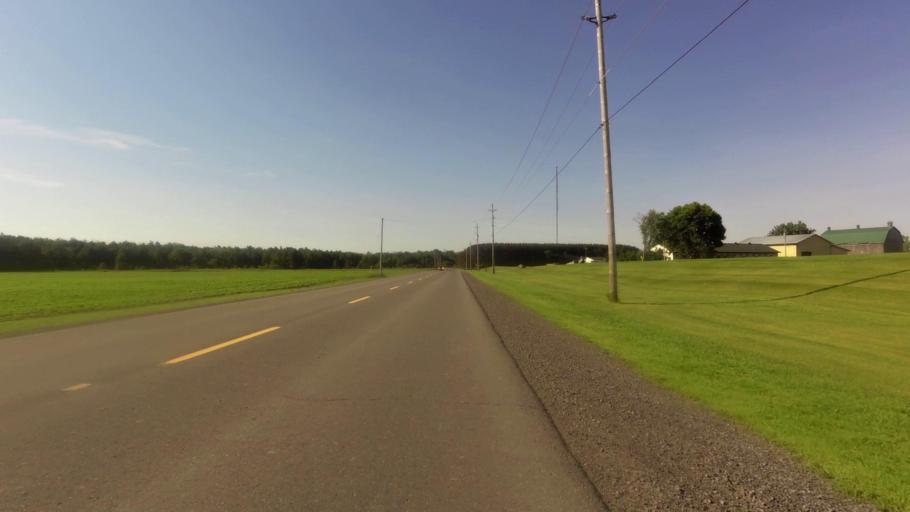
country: CA
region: Ontario
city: Ottawa
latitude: 45.2273
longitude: -75.5609
